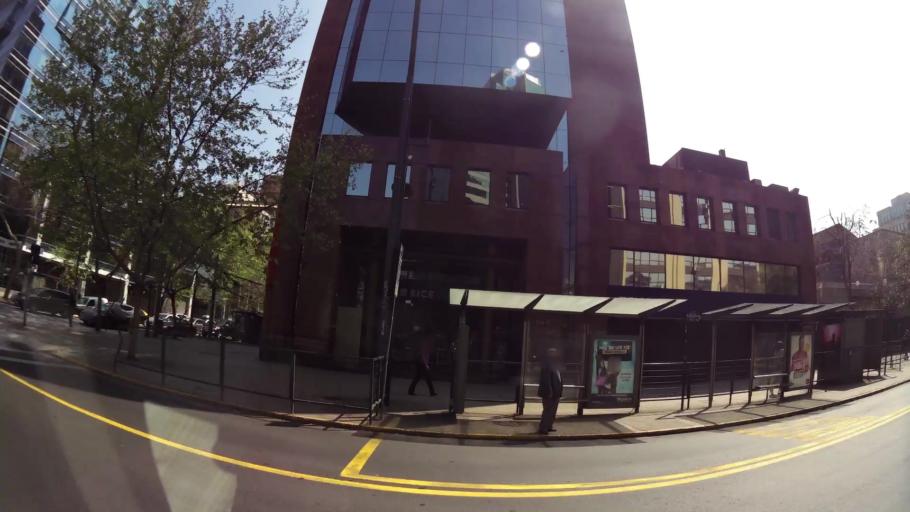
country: CL
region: Santiago Metropolitan
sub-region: Provincia de Santiago
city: Santiago
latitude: -33.4255
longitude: -70.6146
